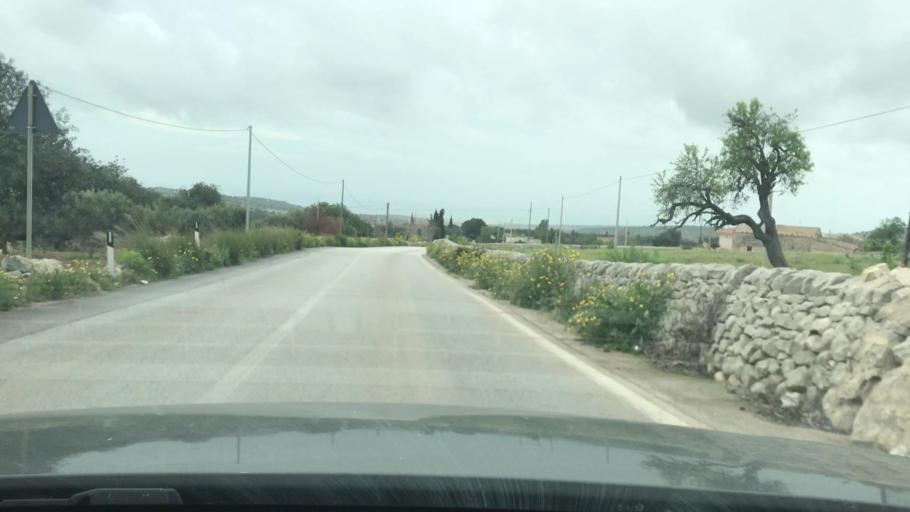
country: IT
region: Sicily
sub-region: Ragusa
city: Scicli
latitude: 36.8056
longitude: 14.7232
